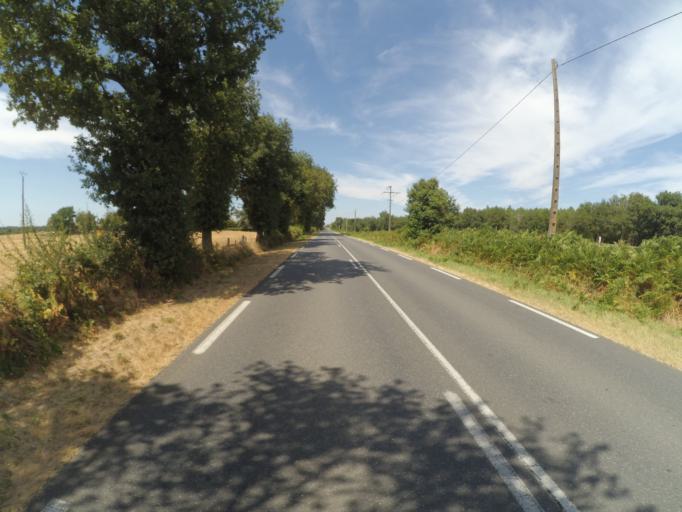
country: FR
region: Poitou-Charentes
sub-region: Departement de la Vienne
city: Availles-Limouzine
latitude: 46.0893
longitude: 0.5858
